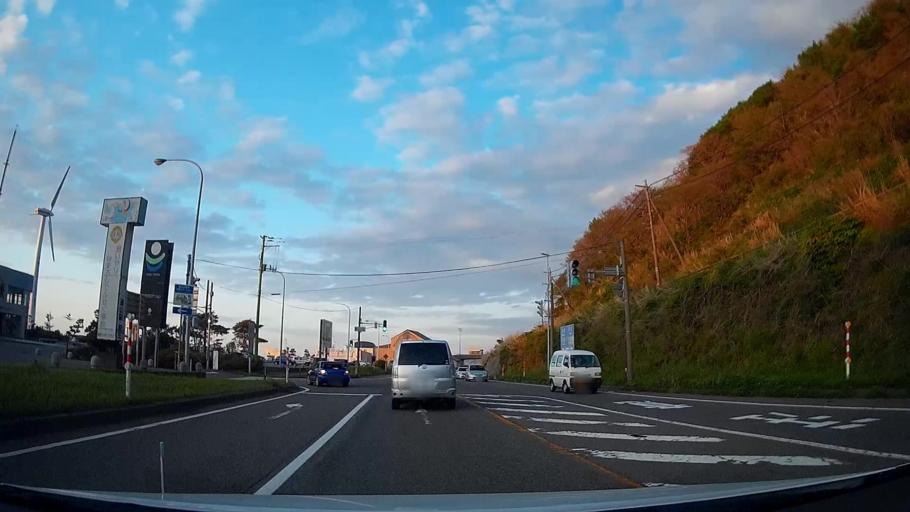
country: JP
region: Niigata
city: Itoigawa
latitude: 37.1133
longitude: 138.0043
